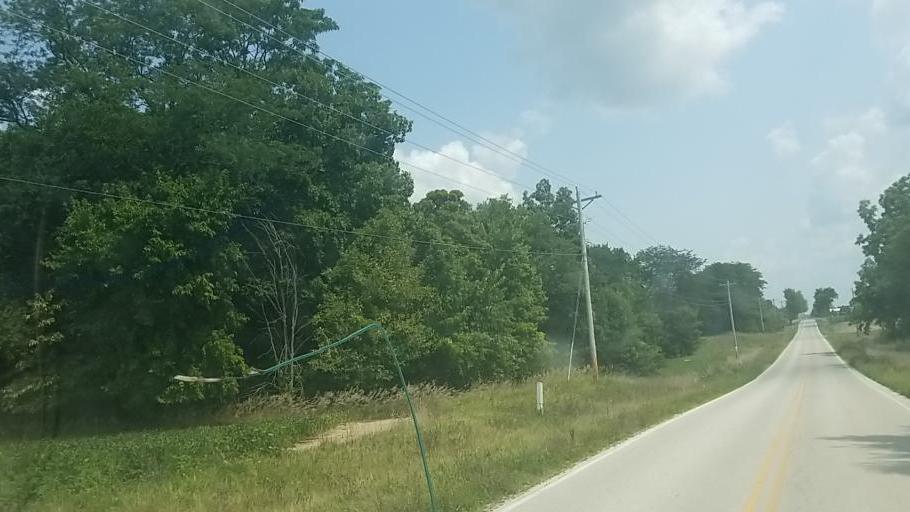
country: US
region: Ohio
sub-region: Wyandot County
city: Carey
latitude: 40.9635
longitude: -83.3323
